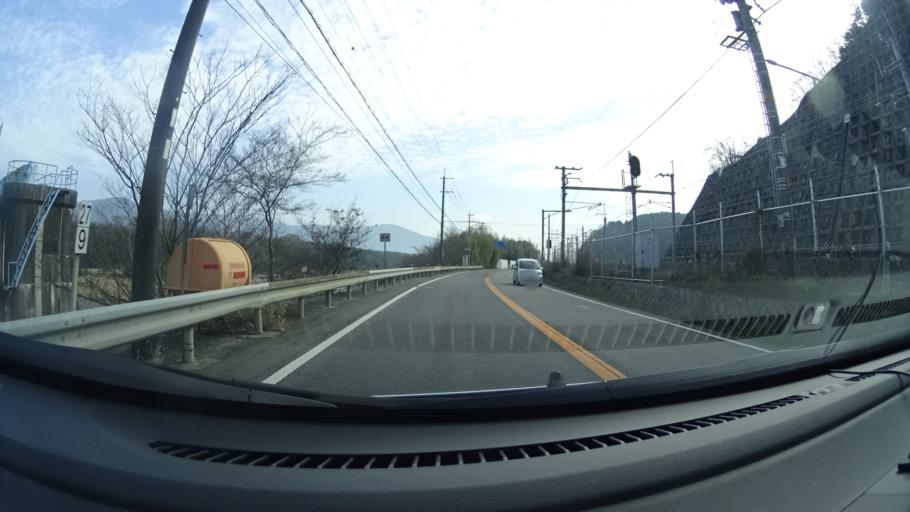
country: JP
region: Kyoto
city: Kameoka
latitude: 35.0663
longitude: 135.5396
